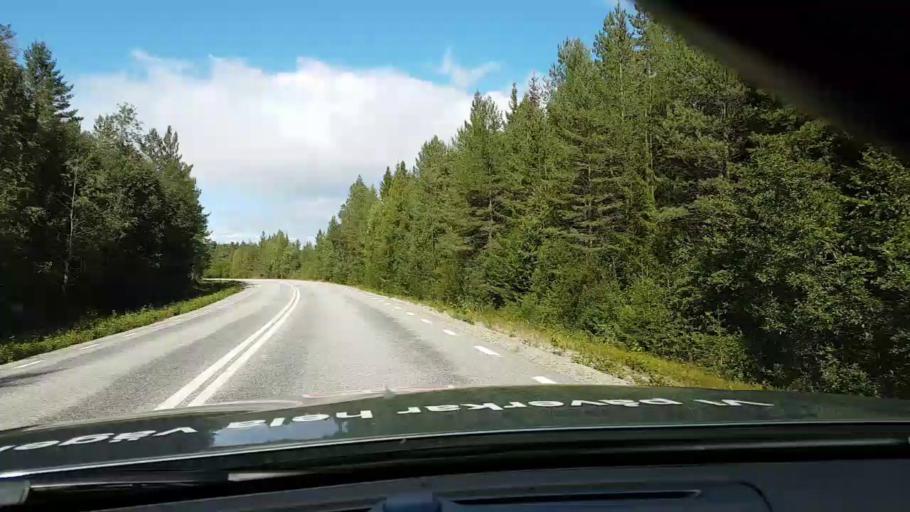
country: SE
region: Vaesternorrland
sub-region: OErnskoeldsviks Kommun
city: Bredbyn
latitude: 63.6313
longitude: 17.9107
